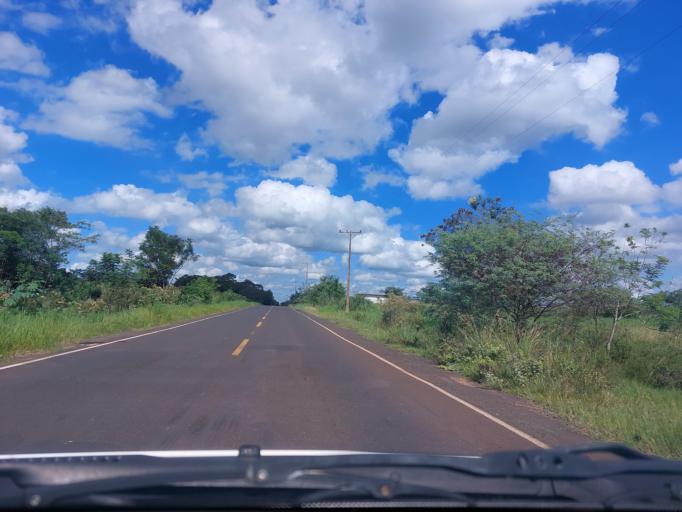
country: PY
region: San Pedro
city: Guayaybi
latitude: -24.5803
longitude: -56.5196
